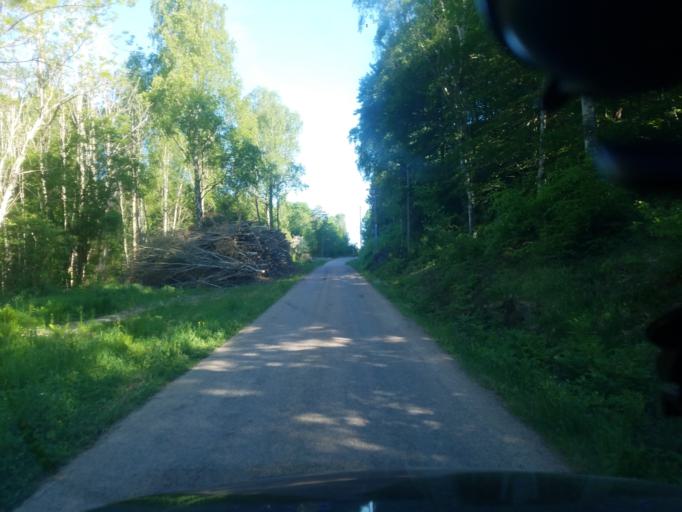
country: SE
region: Vaestra Goetaland
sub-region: Orust
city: Henan
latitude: 58.2794
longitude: 11.6392
